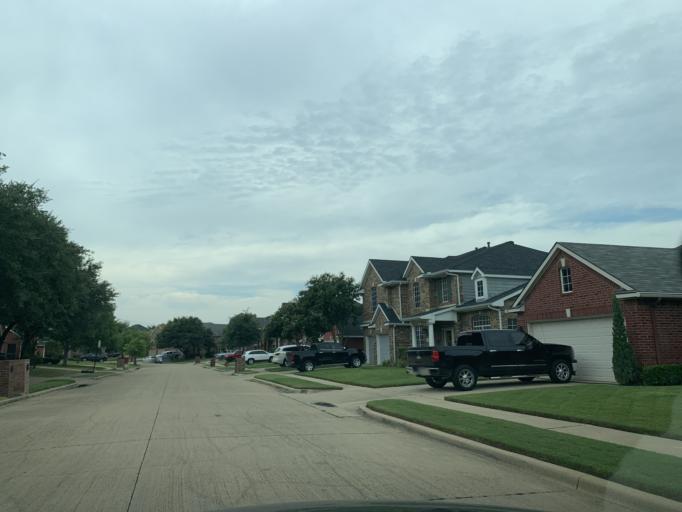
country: US
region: Texas
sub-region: Tarrant County
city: Watauga
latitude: 32.8511
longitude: -97.2879
